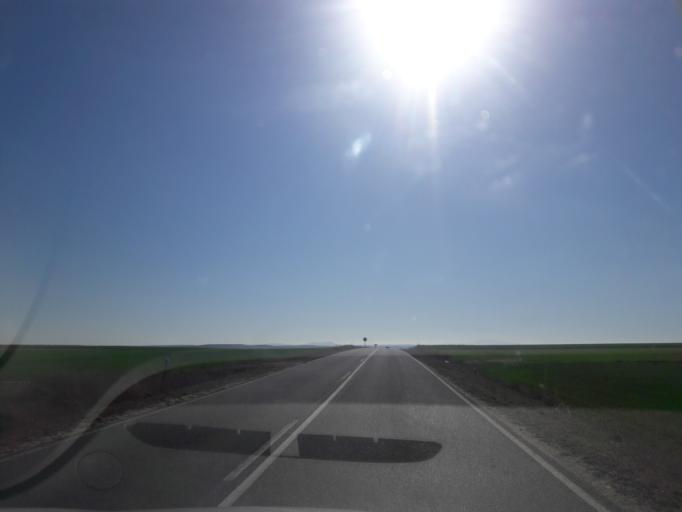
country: ES
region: Castille and Leon
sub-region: Provincia de Salamanca
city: Macotera
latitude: 40.8224
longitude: -5.2677
